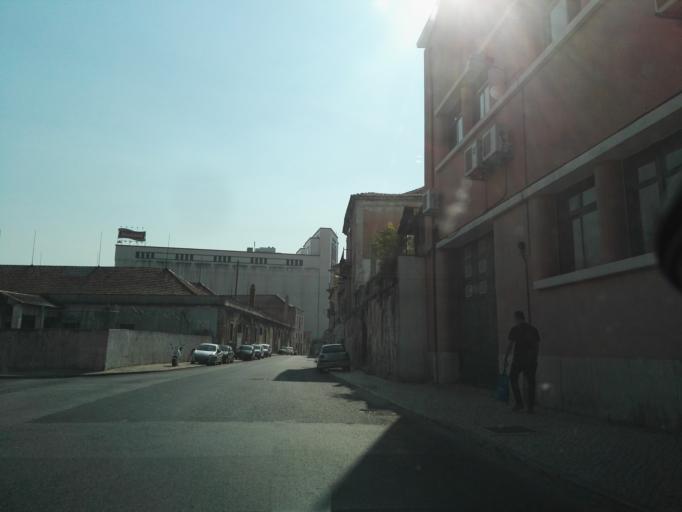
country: PT
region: Lisbon
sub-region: Lisbon
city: Lisbon
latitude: 38.7361
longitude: -9.1041
